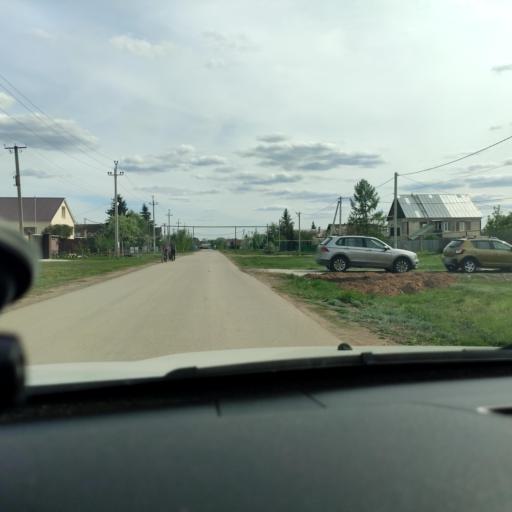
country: RU
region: Samara
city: Kinel'
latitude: 53.1601
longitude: 50.6422
